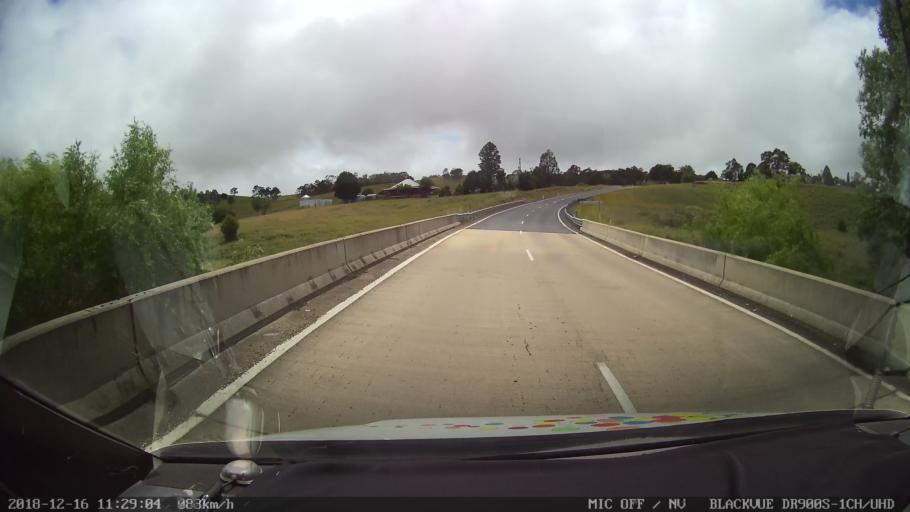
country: AU
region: New South Wales
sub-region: Tenterfield Municipality
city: Carrolls Creek
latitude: -29.0352
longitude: 152.1042
